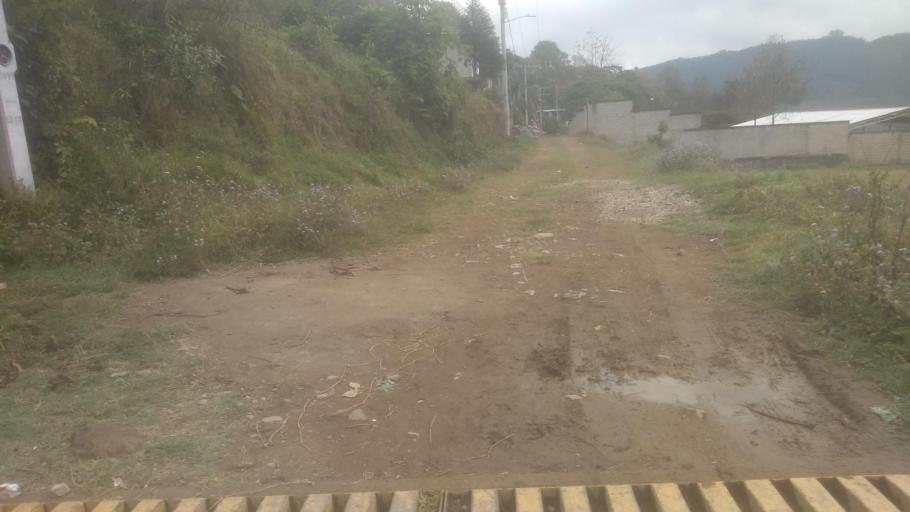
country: MX
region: Veracruz
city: Chocaman
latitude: 18.9885
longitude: -97.0580
